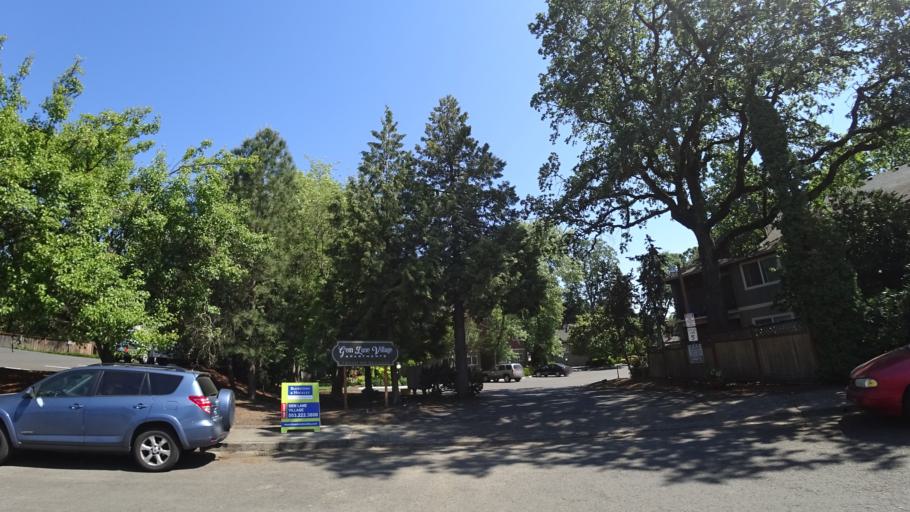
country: US
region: Oregon
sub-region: Washington County
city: Cedar Hills
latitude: 45.4988
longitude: -122.8056
